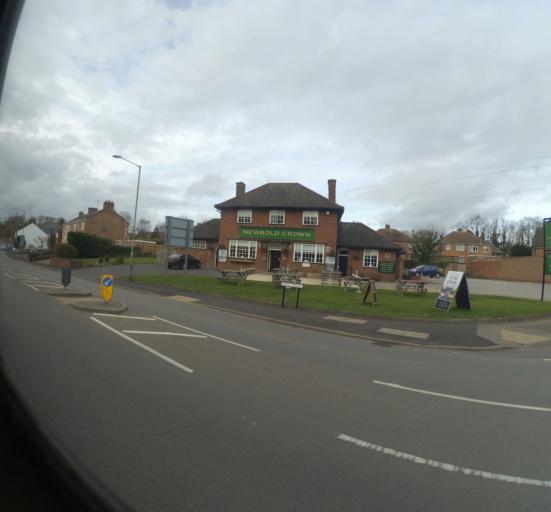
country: GB
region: England
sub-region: Warwickshire
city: Rugby
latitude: 52.3901
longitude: -1.2803
